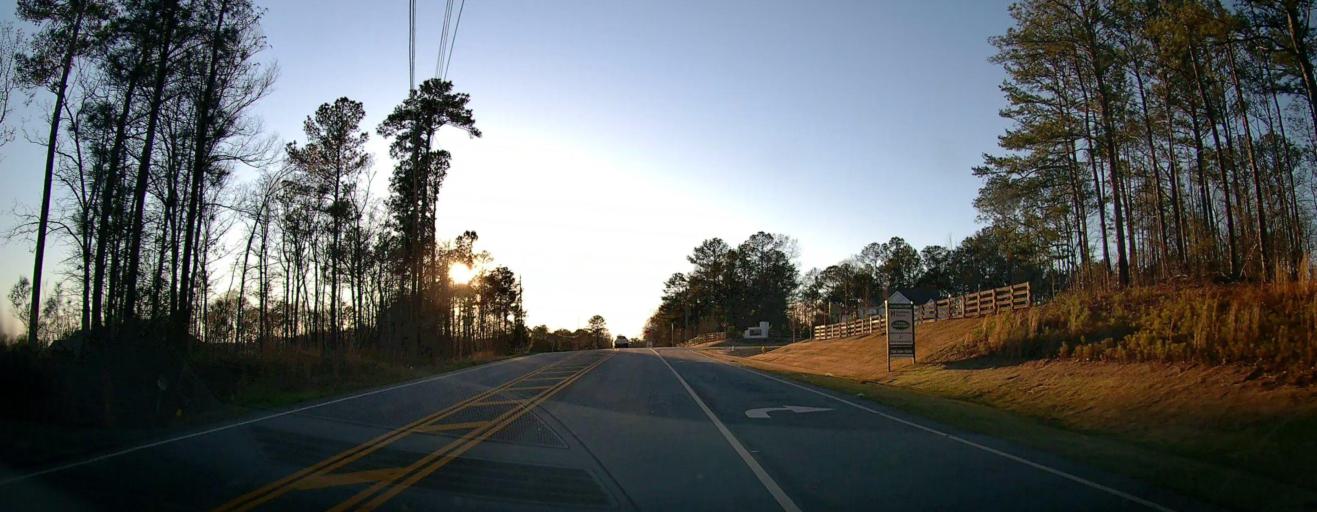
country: US
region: Georgia
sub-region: Harris County
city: Hamilton
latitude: 32.6678
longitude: -84.9685
